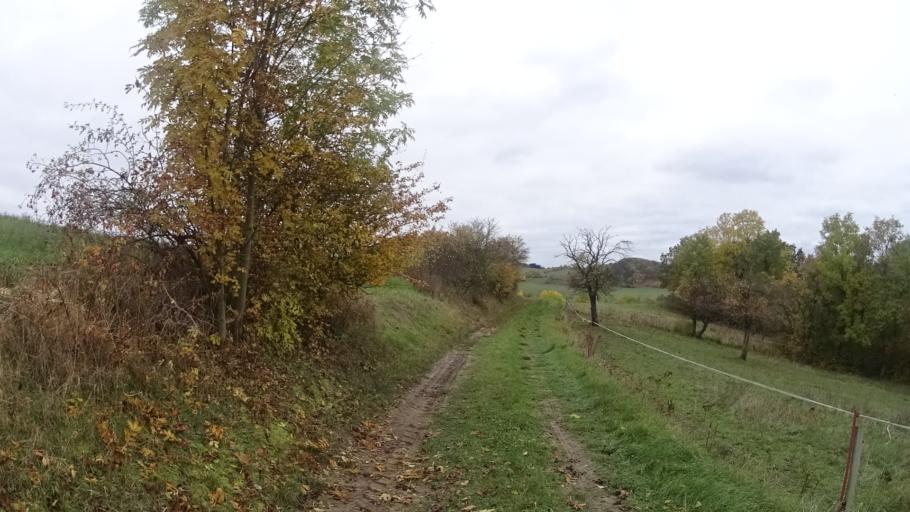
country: DE
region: Thuringia
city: Apfelstadt
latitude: 50.8592
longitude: 10.8964
